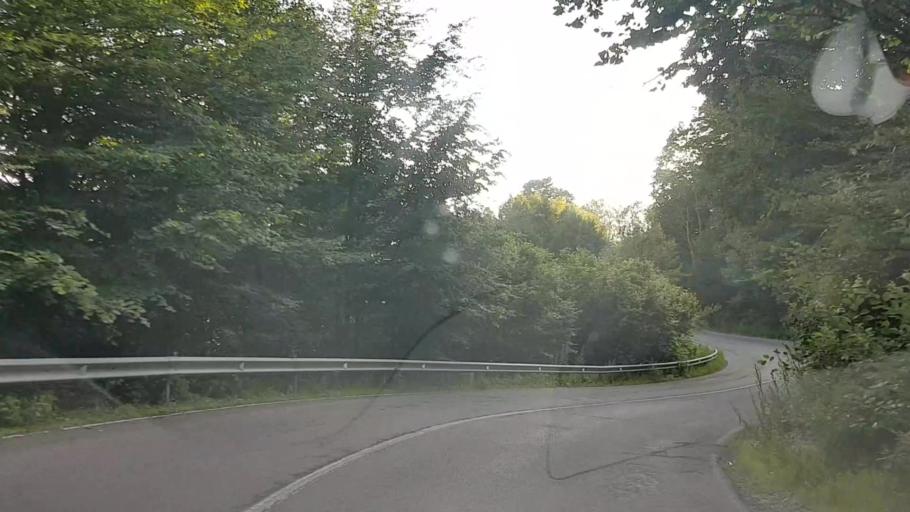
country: RO
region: Harghita
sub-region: Comuna Praid
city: Ocna de Sus
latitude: 46.5704
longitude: 25.1899
